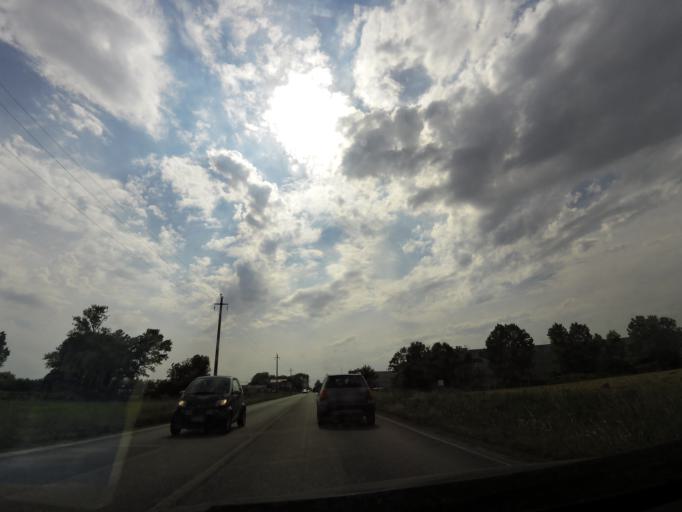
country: IT
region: Lombardy
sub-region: Citta metropolitana di Milano
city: Carpiano
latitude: 45.3498
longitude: 9.2883
